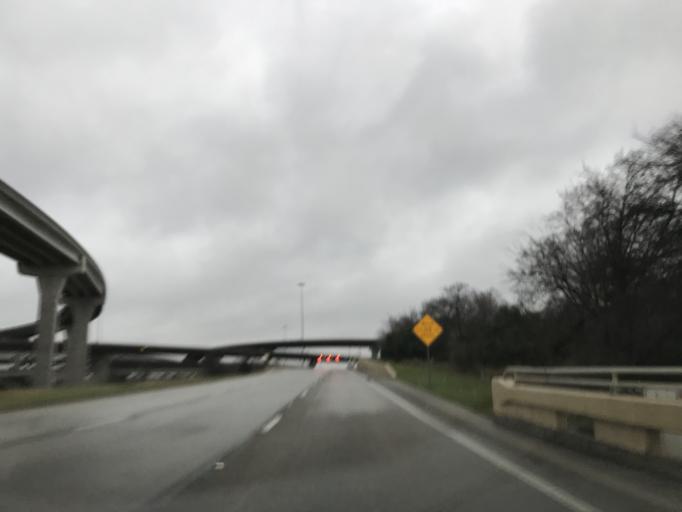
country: US
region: Texas
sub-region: Dallas County
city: Grand Prairie
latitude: 32.7620
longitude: -97.0301
